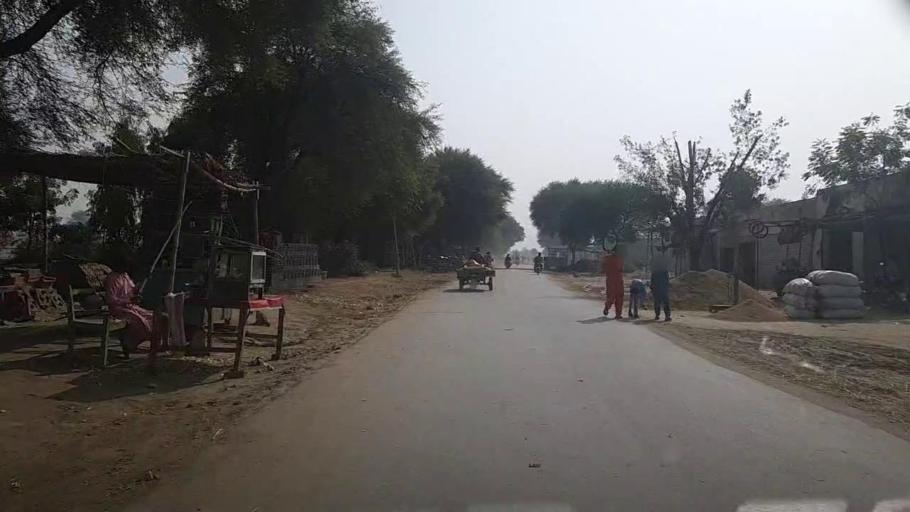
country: PK
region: Sindh
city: Kashmor
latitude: 28.4222
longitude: 69.5710
